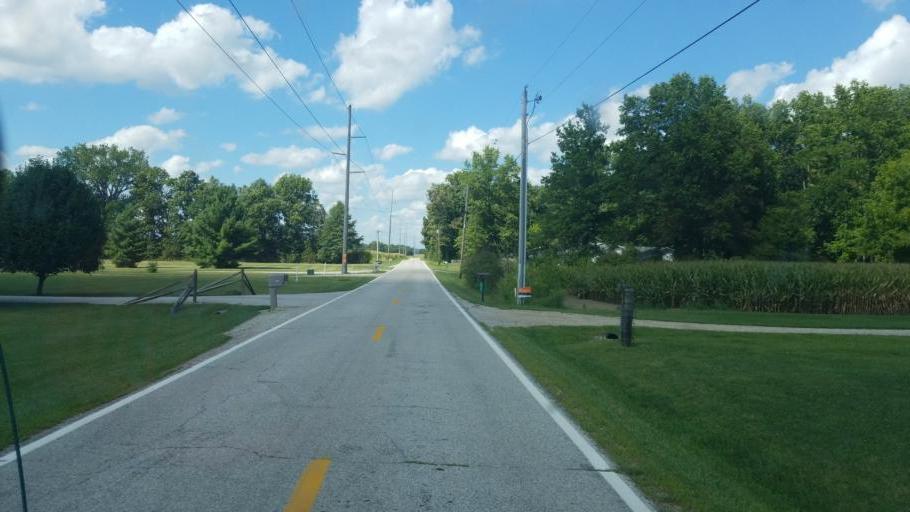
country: US
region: Ohio
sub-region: Marion County
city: Prospect
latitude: 40.3264
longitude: -83.2035
